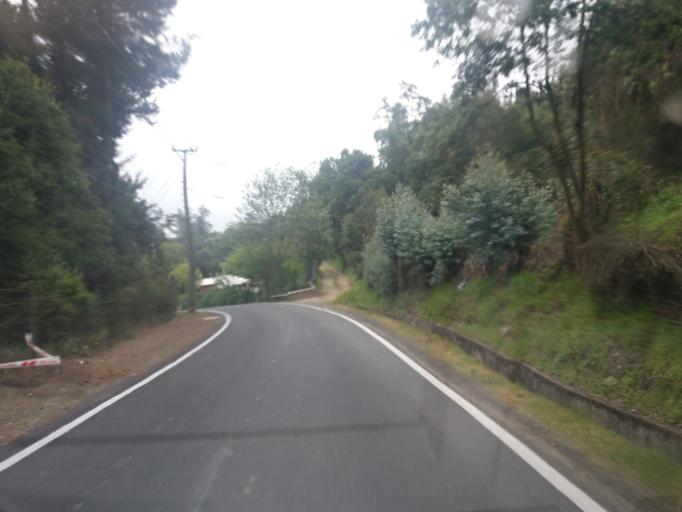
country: CL
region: Valparaiso
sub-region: Provincia de Marga Marga
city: Limache
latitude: -33.0186
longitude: -71.0699
